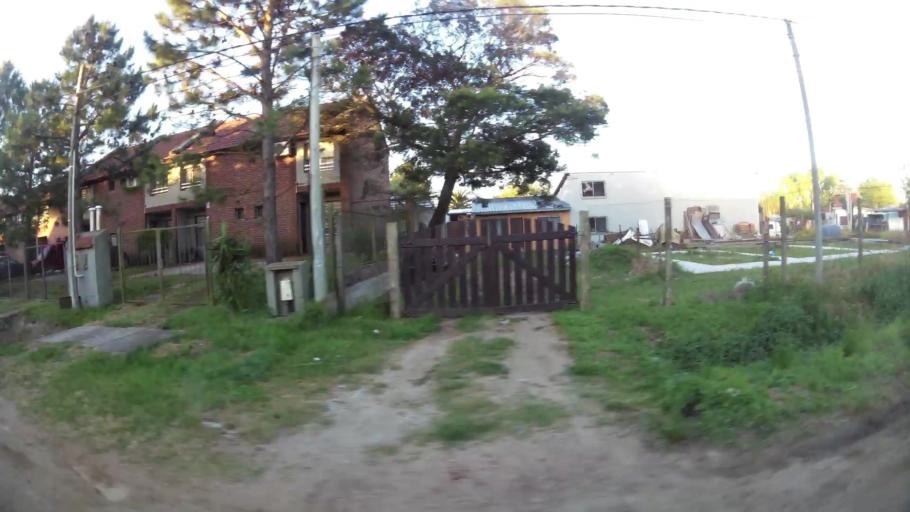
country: UY
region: Canelones
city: Barra de Carrasco
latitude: -34.8370
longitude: -55.9990
